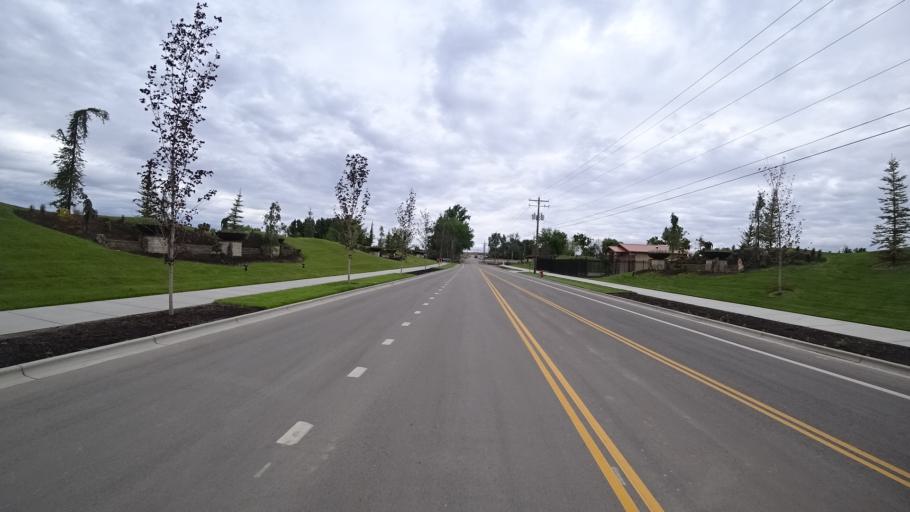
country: US
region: Idaho
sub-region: Ada County
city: Star
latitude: 43.7058
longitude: -116.4435
